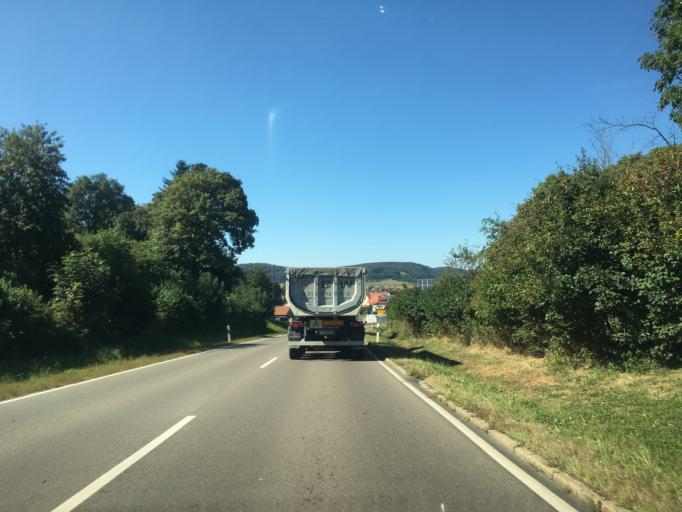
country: DE
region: Baden-Wuerttemberg
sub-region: Tuebingen Region
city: Sankt Johann
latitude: 48.3830
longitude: 9.3046
